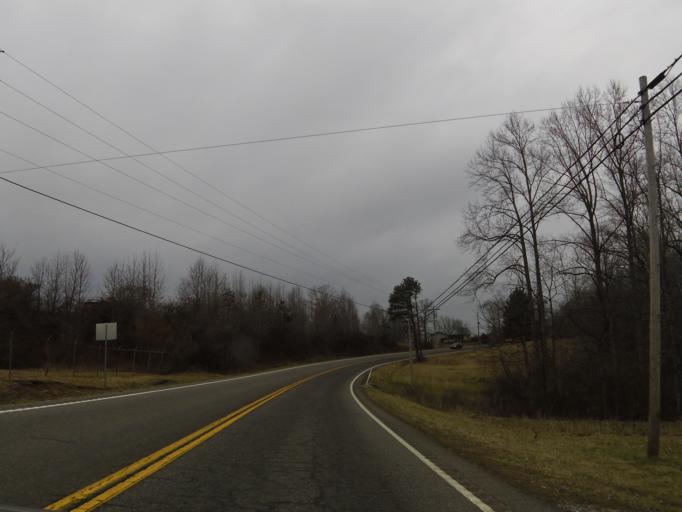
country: US
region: Tennessee
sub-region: Morgan County
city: Wartburg
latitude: 36.1647
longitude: -84.6553
